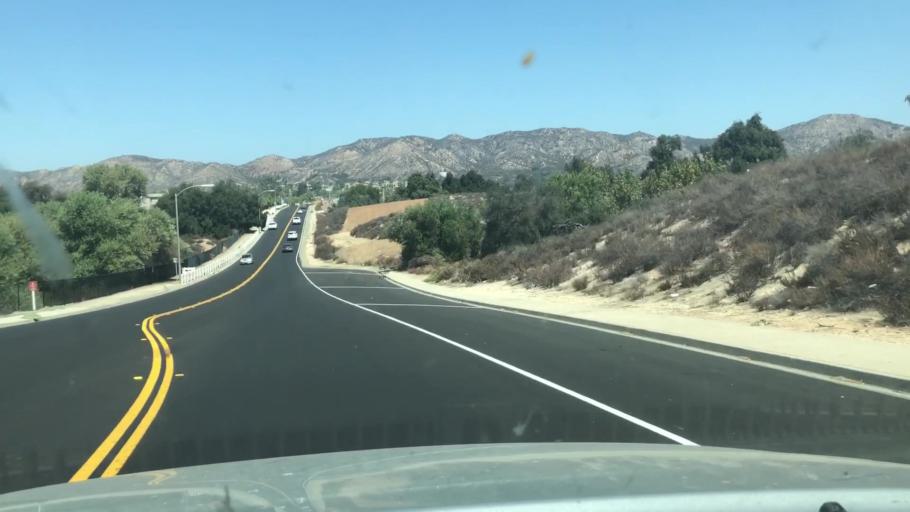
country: US
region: California
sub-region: Riverside County
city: Wildomar
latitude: 33.5933
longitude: -117.2368
